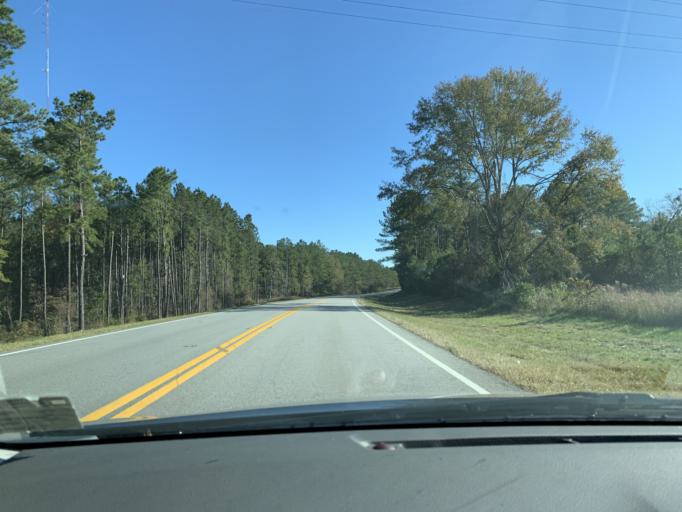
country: US
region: Georgia
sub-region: Ben Hill County
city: Fitzgerald
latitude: 31.7777
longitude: -83.0861
